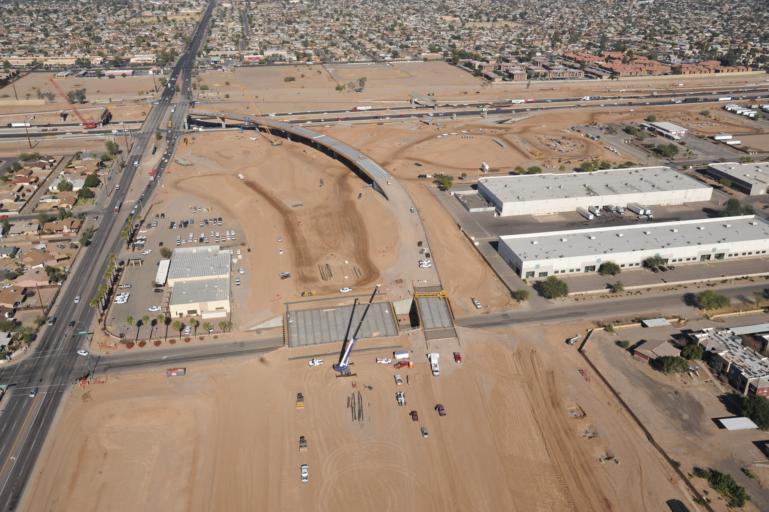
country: US
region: Arizona
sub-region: Maricopa County
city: Tolleson
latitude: 33.4565
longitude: -112.1856
